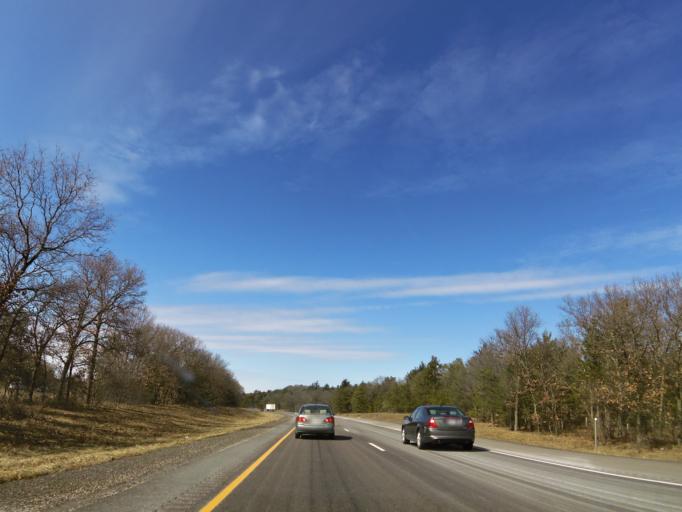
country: US
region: Wisconsin
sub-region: Monroe County
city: Tomah
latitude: 44.1505
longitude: -90.5510
